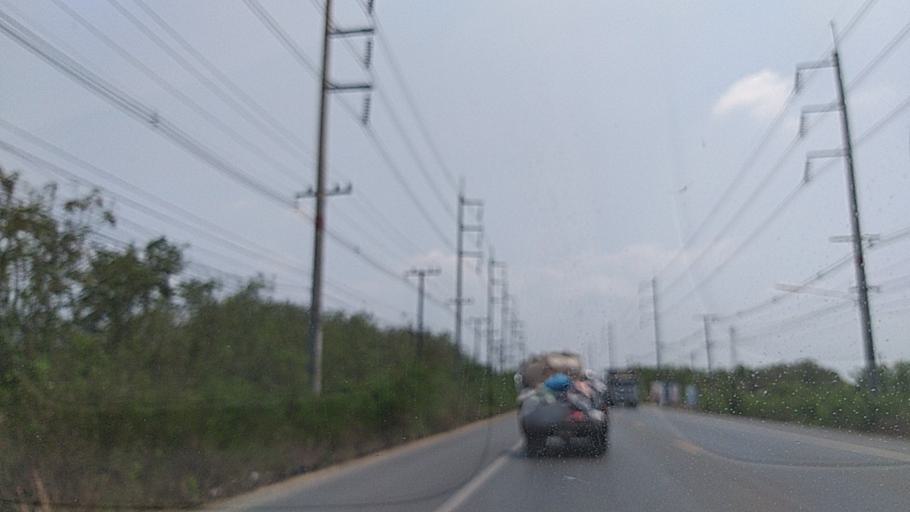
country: TH
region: Chachoengsao
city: Bang Nam Priao
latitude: 13.7874
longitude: 101.0558
